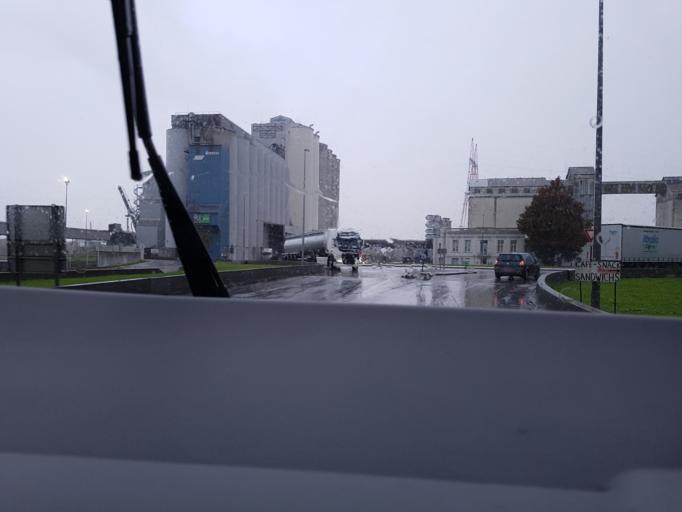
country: FR
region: Aquitaine
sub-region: Departement de la Gironde
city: Bassens
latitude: 44.9143
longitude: -0.5415
